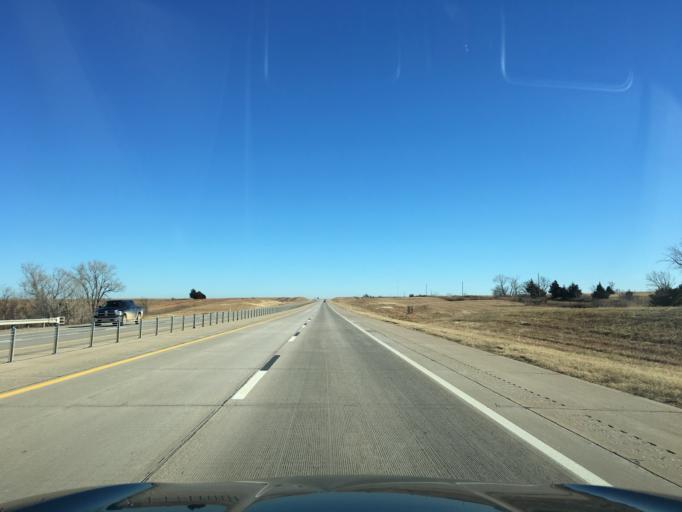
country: US
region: Oklahoma
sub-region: Noble County
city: Perry
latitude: 36.3920
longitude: -97.1650
